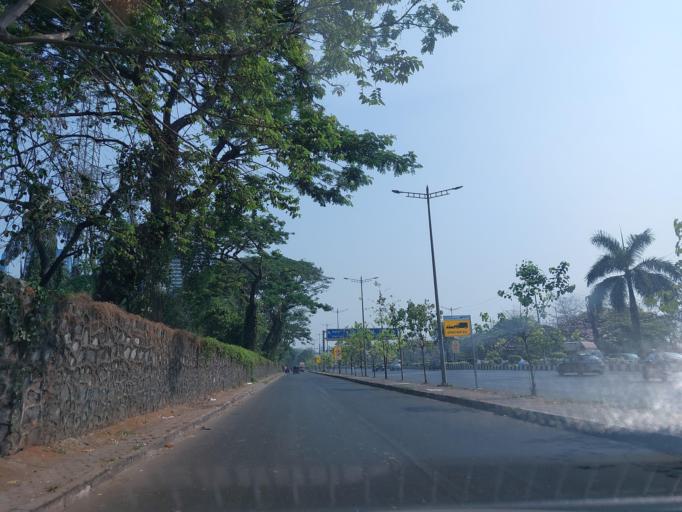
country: IN
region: Maharashtra
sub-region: Mumbai Suburban
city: Powai
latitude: 19.0988
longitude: 72.9279
